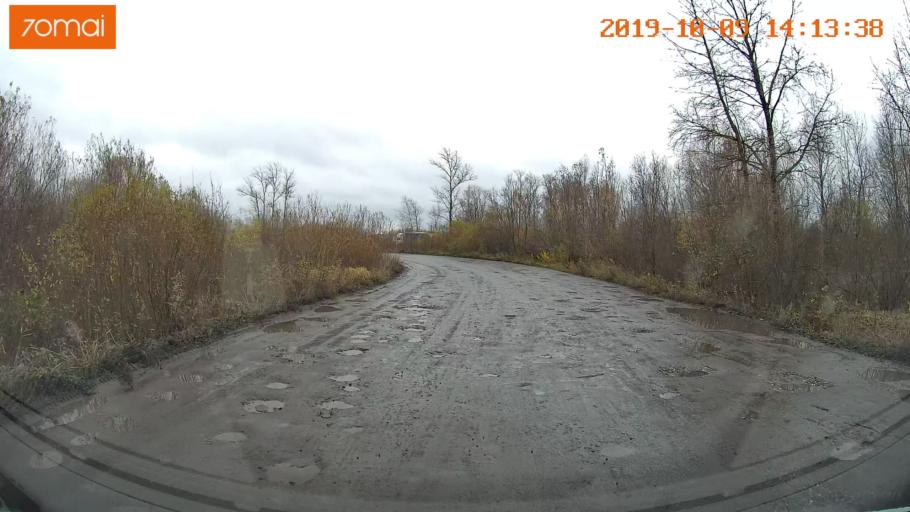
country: RU
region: Kostroma
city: Buy
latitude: 58.4807
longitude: 41.5116
